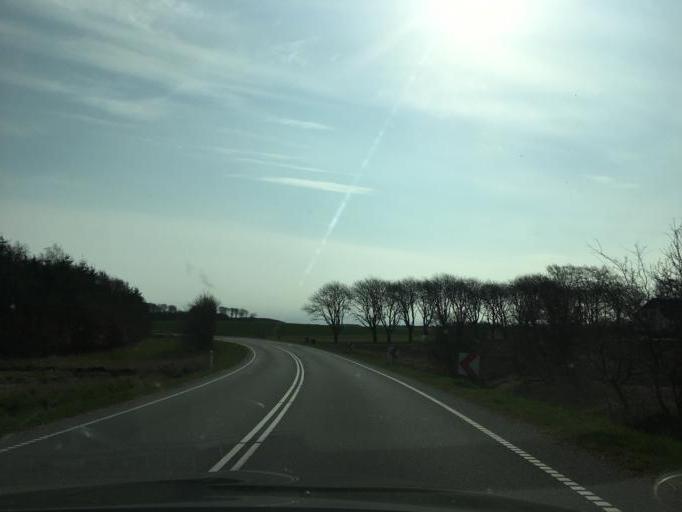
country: DK
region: South Denmark
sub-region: Vejen Kommune
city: Brorup
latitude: 55.4949
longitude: 9.0453
